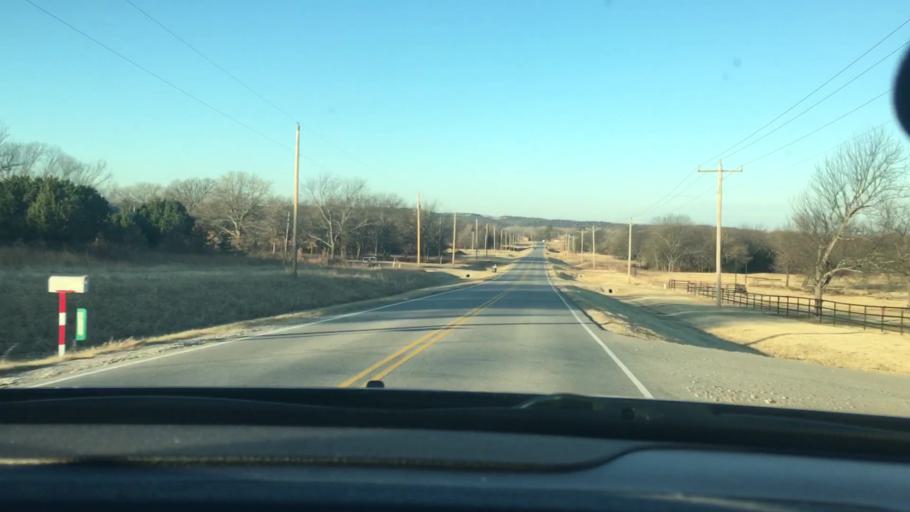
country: US
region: Oklahoma
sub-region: Murray County
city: Davis
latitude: 34.4774
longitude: -97.1210
